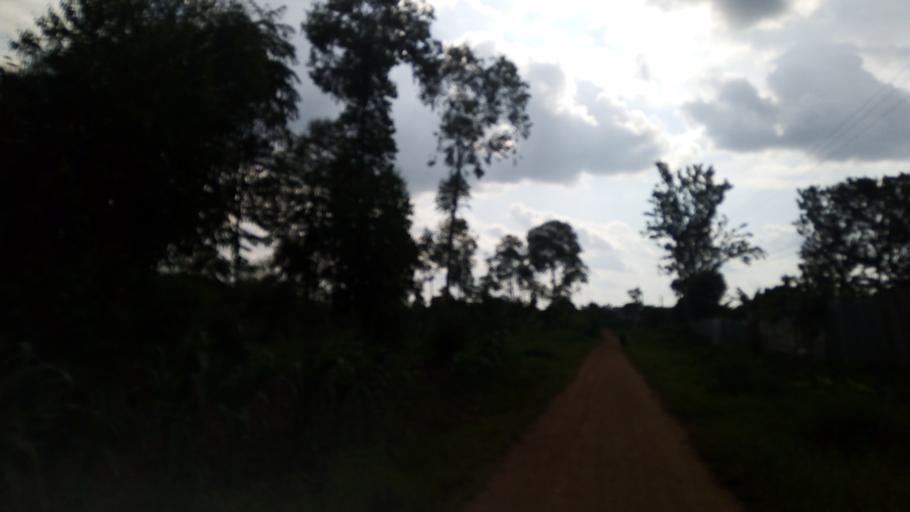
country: UG
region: Eastern Region
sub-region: Mbale District
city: Mbale
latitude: 1.0755
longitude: 34.1561
